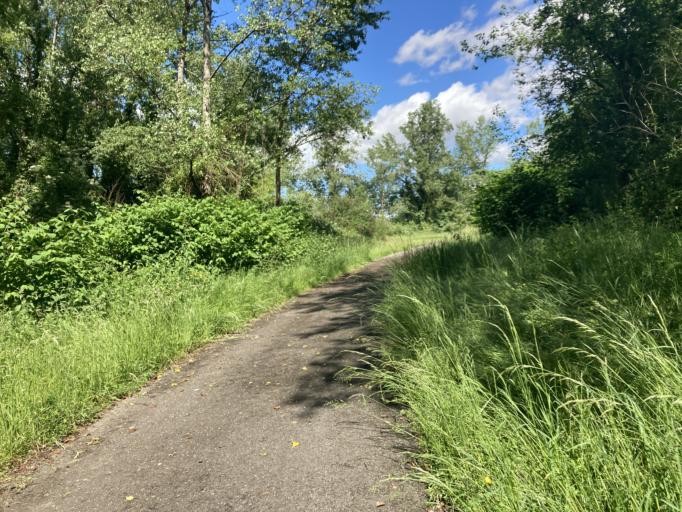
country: FR
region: Aquitaine
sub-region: Departement des Pyrenees-Atlantiques
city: Arbus
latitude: 43.3330
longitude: -0.4878
